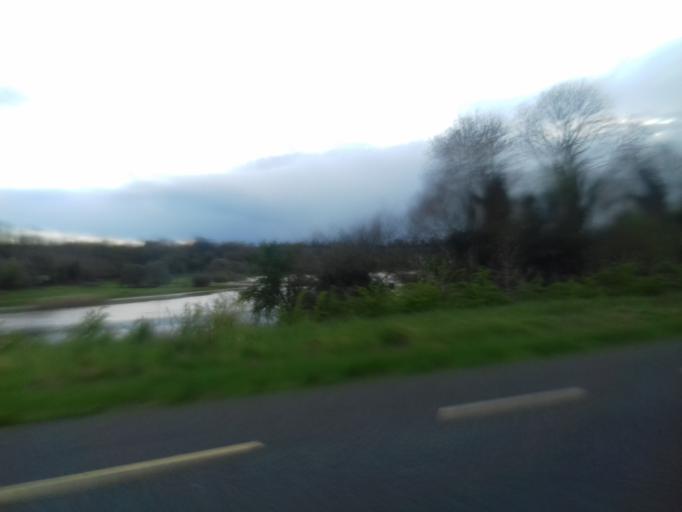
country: IE
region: Ulster
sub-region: An Cabhan
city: Belturbet
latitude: 54.0774
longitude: -7.4226
